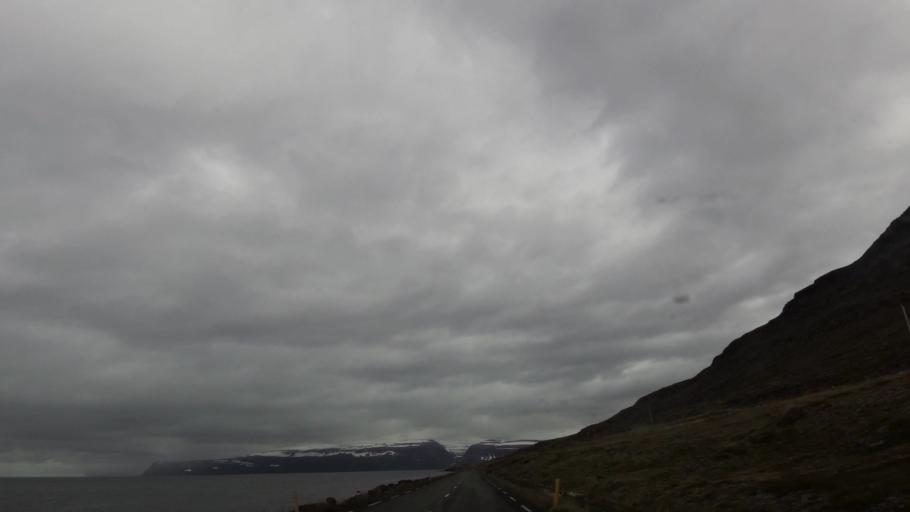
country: IS
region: Westfjords
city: Isafjoerdur
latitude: 66.0326
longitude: -22.7744
